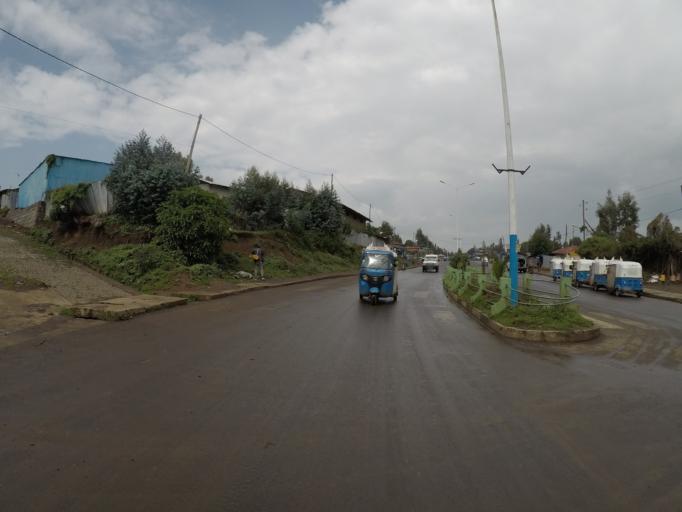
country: ET
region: Amhara
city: Debark'
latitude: 13.1520
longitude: 37.8960
